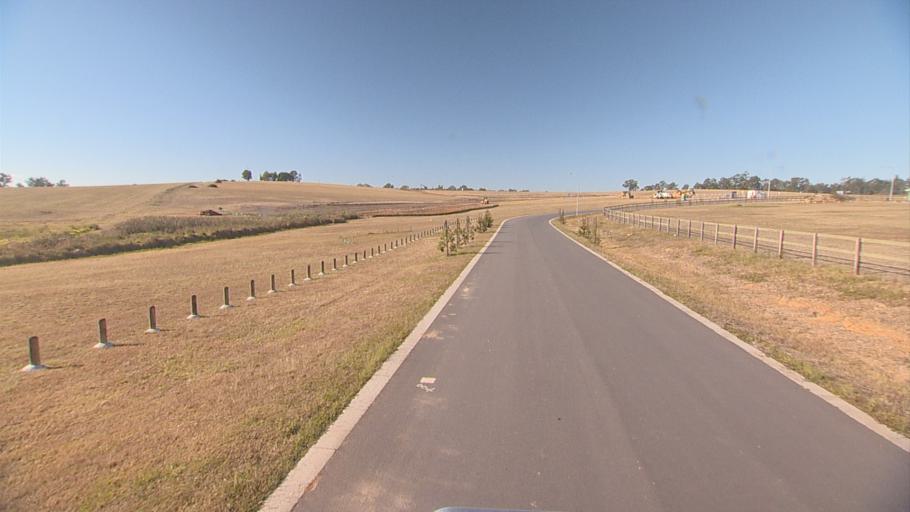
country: AU
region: Queensland
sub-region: Logan
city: North Maclean
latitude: -27.8098
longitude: 152.9953
